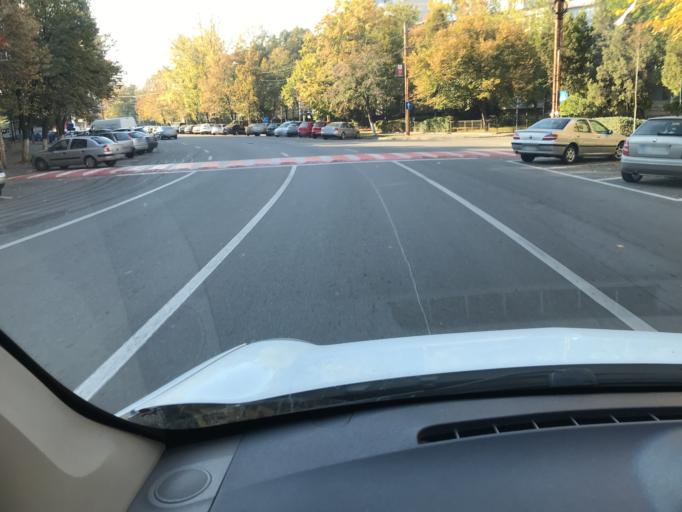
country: RO
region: Olt
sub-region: Municipiul Slatina
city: Slatina
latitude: 44.4341
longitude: 24.3691
